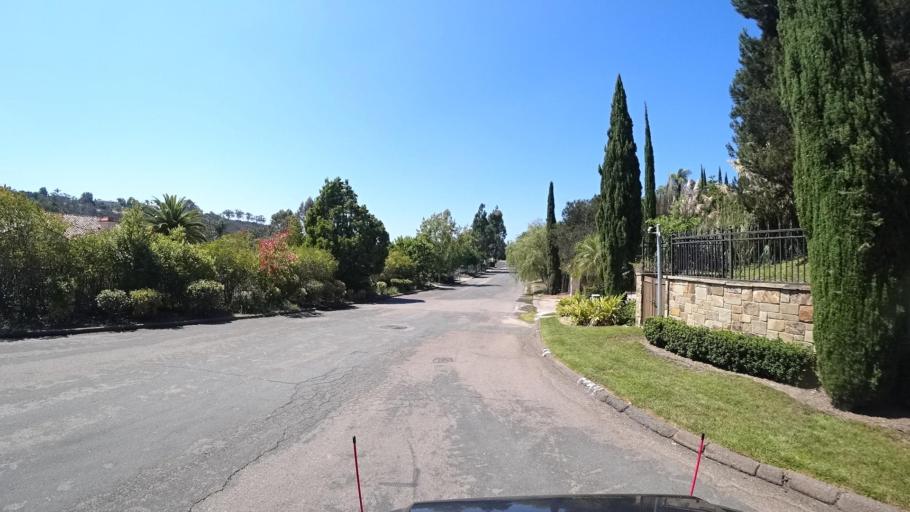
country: US
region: California
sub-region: San Diego County
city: Fairbanks Ranch
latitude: 32.9794
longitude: -117.1707
